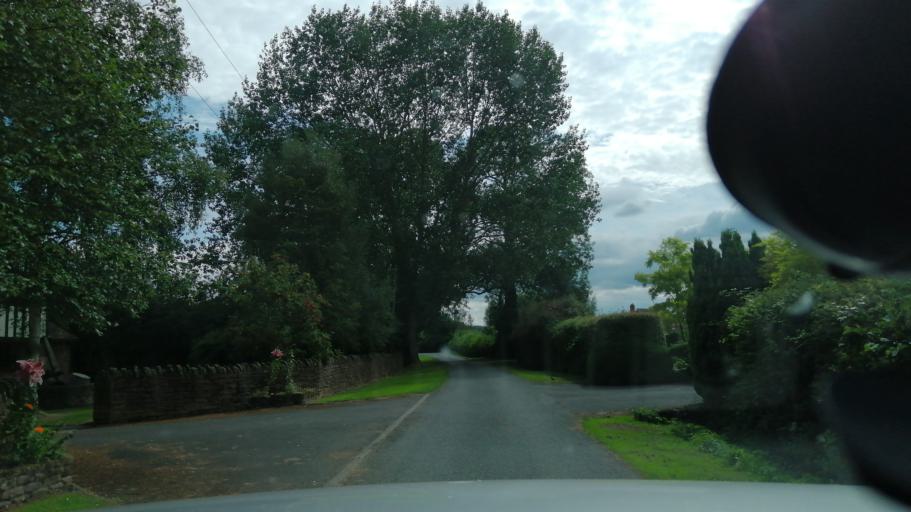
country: GB
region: England
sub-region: Herefordshire
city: Thruxton
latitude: 52.0101
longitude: -2.7958
